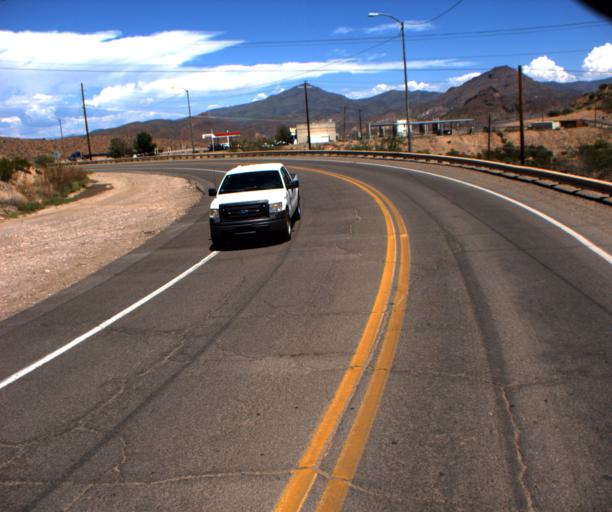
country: US
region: Arizona
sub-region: Greenlee County
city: Clifton
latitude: 33.0507
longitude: -109.3240
